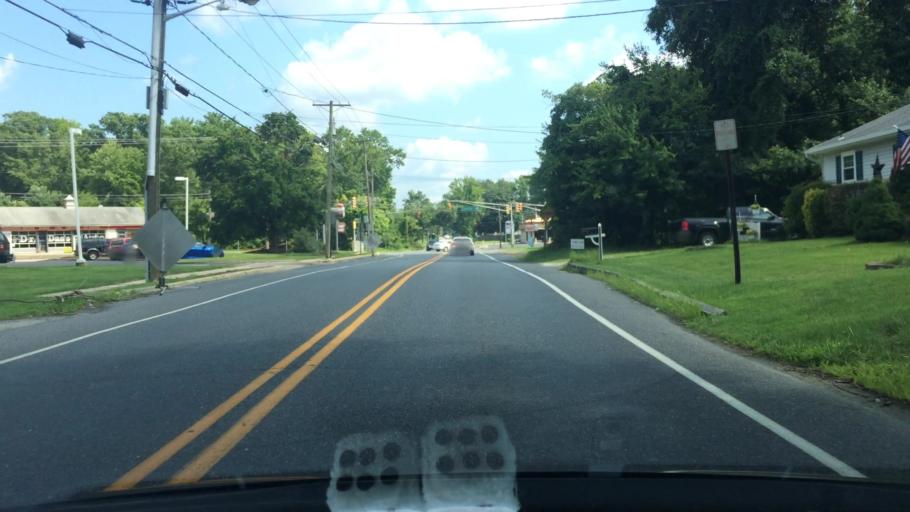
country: US
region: New Jersey
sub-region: Camden County
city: Blackwood
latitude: 39.8064
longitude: -75.0957
